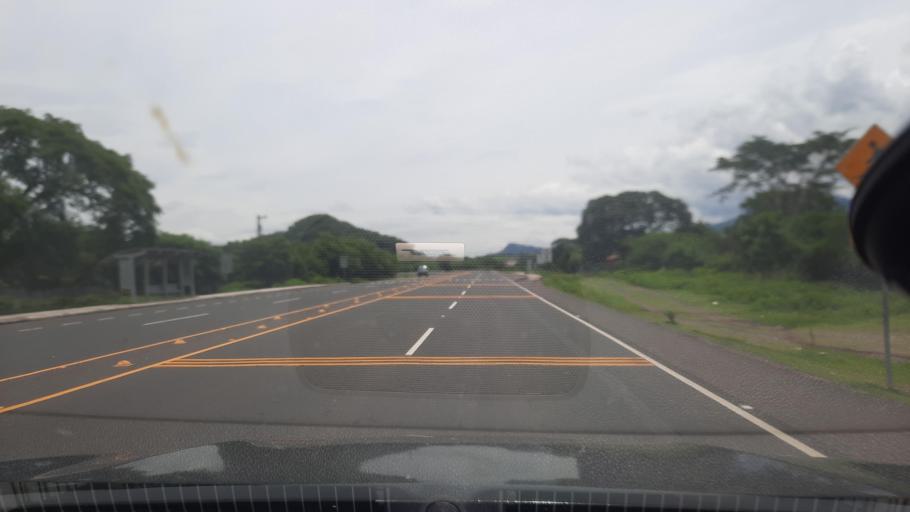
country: HN
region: Valle
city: Aramecina
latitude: 13.7225
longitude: -87.7101
